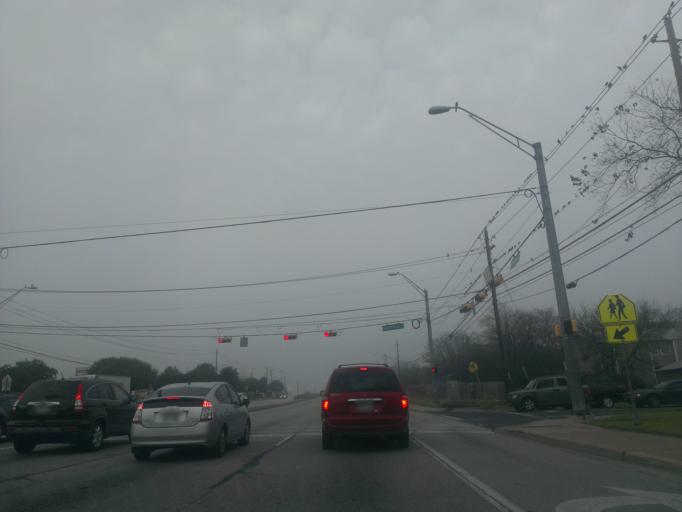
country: US
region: Texas
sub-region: Travis County
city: Wells Branch
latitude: 30.4157
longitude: -97.6955
